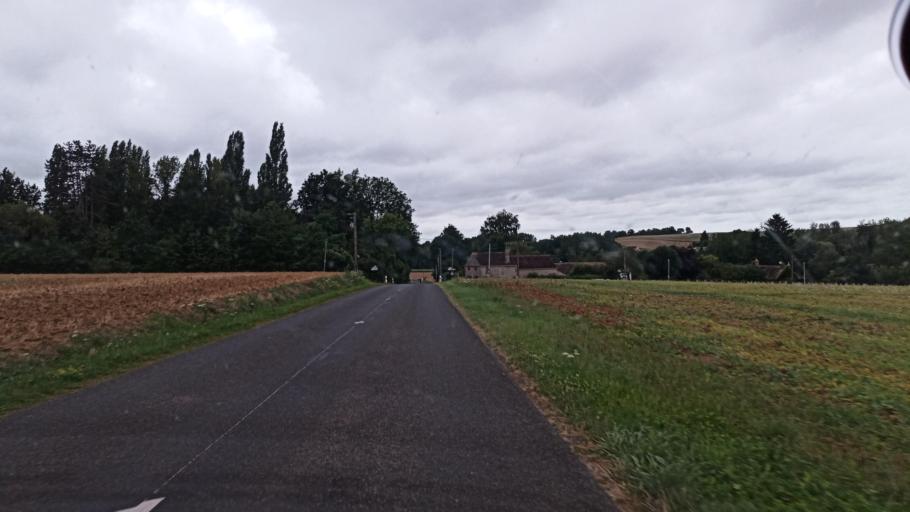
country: FR
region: Bourgogne
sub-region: Departement de l'Yonne
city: Cheroy
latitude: 48.2507
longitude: 3.0300
